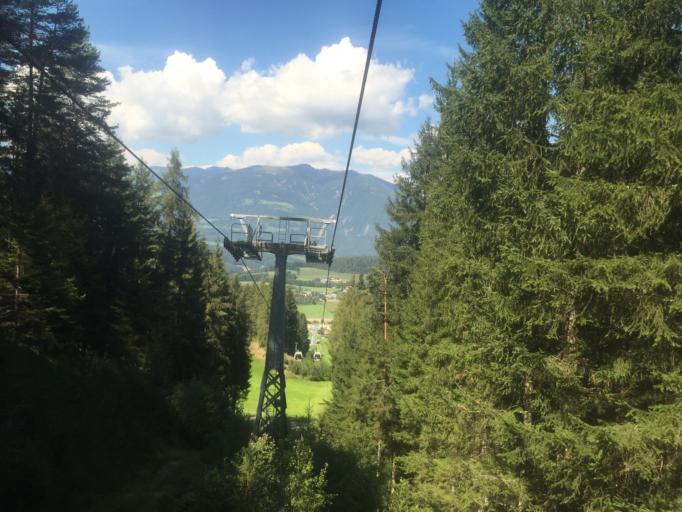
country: IT
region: Trentino-Alto Adige
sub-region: Bolzano
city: Riscone
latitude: 46.7636
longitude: 11.9451
